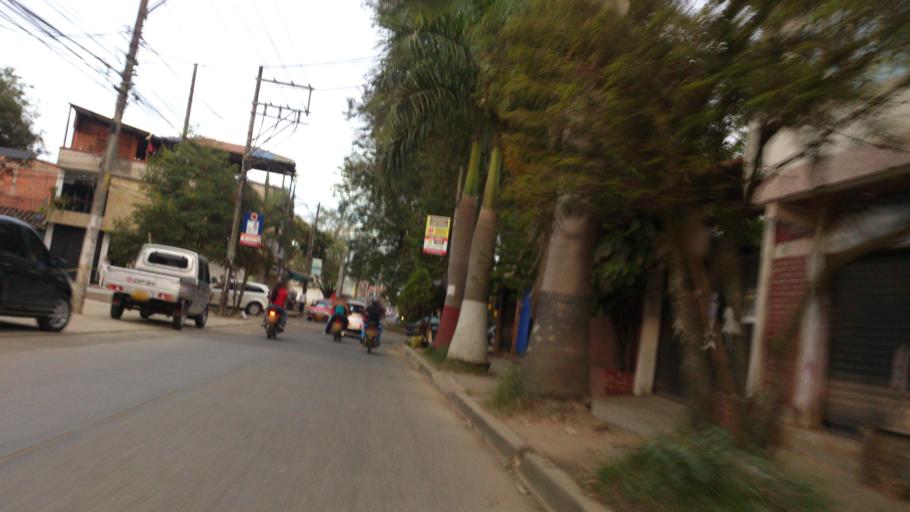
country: CO
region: Valle del Cauca
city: Jamundi
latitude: 3.2579
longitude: -76.5456
